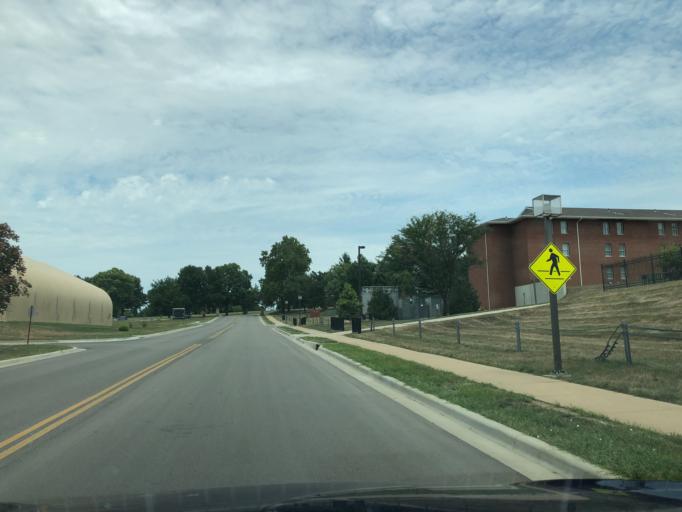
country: US
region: Kansas
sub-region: Leavenworth County
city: Leavenworth
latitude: 39.3419
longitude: -94.9239
